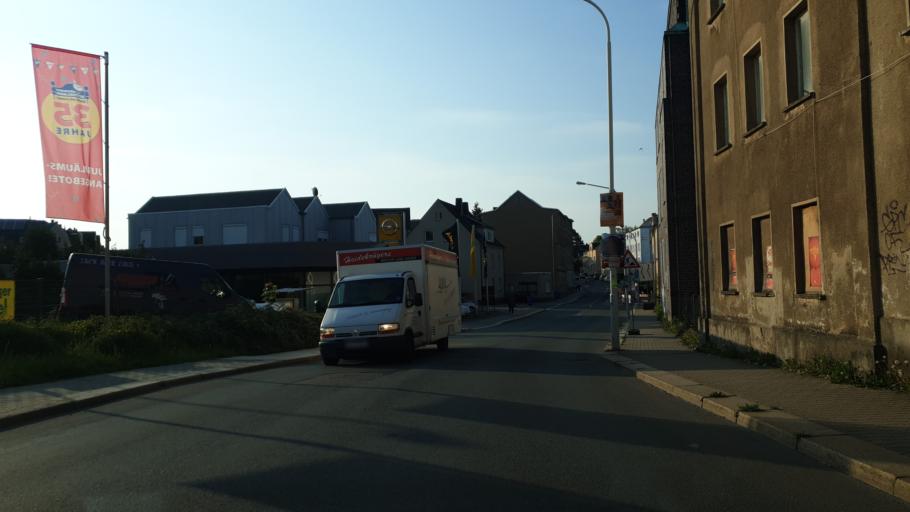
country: DE
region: Saxony
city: Limbach-Oberfrohna
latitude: 50.8581
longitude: 12.7706
